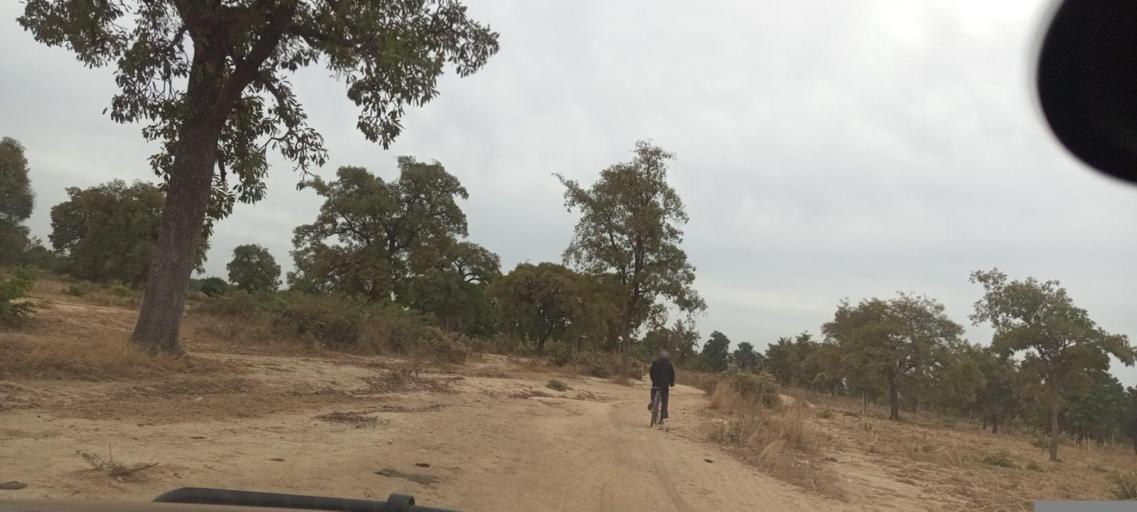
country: ML
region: Koulikoro
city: Kati
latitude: 12.7940
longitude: -8.2532
